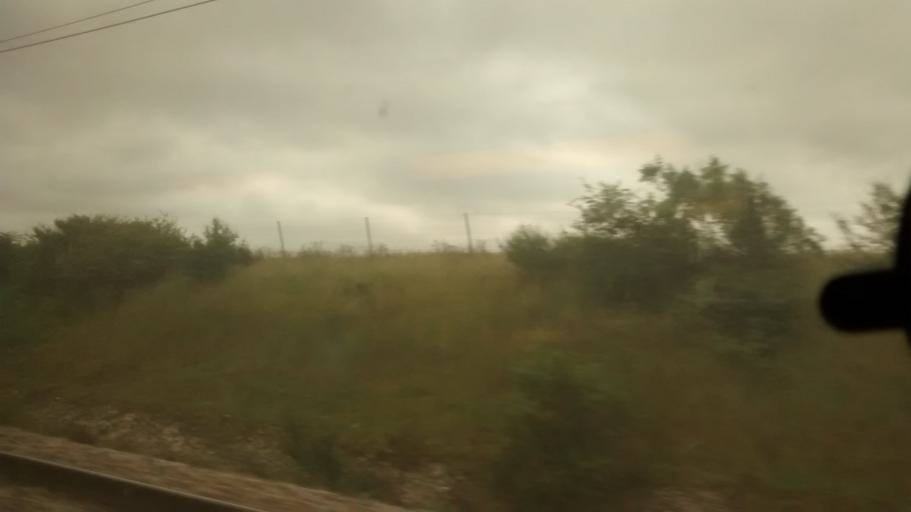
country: FR
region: Centre
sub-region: Departement d'Eure-et-Loir
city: Voves
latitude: 48.2677
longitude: 1.6007
